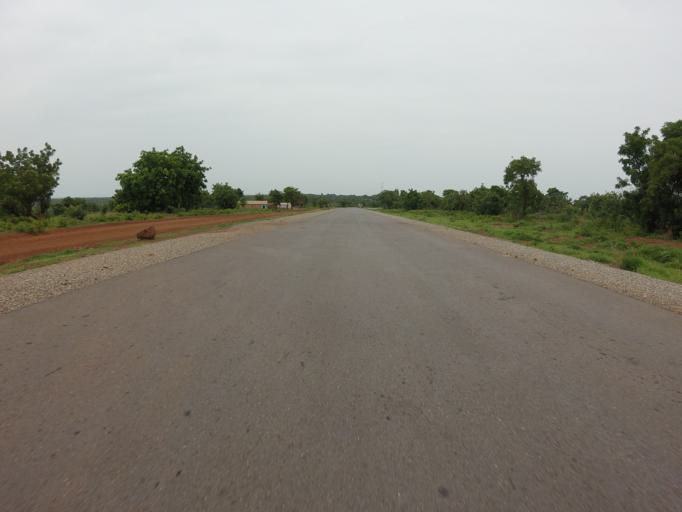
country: GH
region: Northern
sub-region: Yendi
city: Yendi
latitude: 9.2982
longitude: 0.0195
